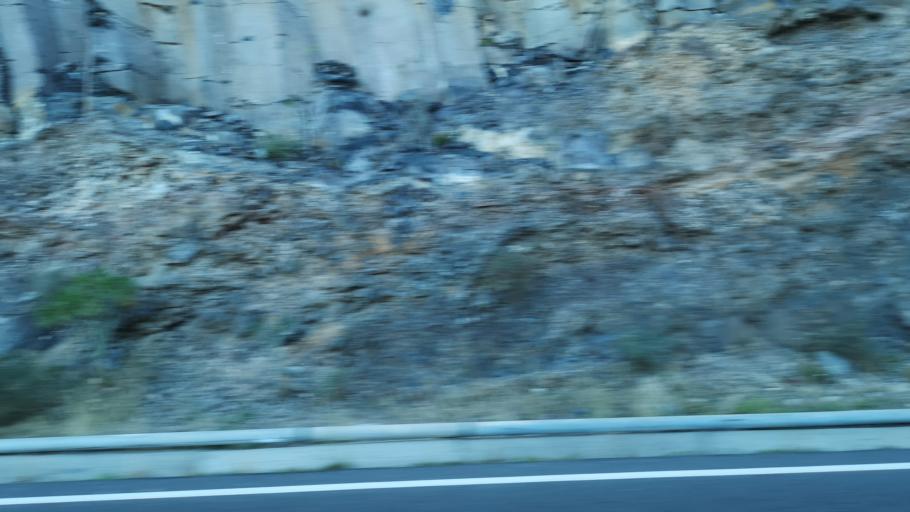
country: ES
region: Canary Islands
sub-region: Provincia de Santa Cruz de Tenerife
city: Alajero
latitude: 28.0320
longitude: -17.2046
